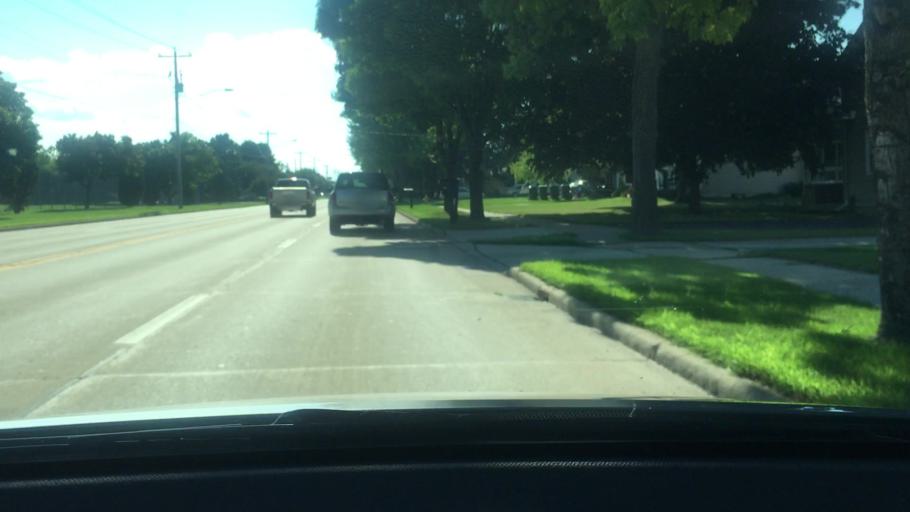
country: US
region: Wisconsin
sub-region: Winnebago County
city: Oshkosh
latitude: 43.9960
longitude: -88.5594
